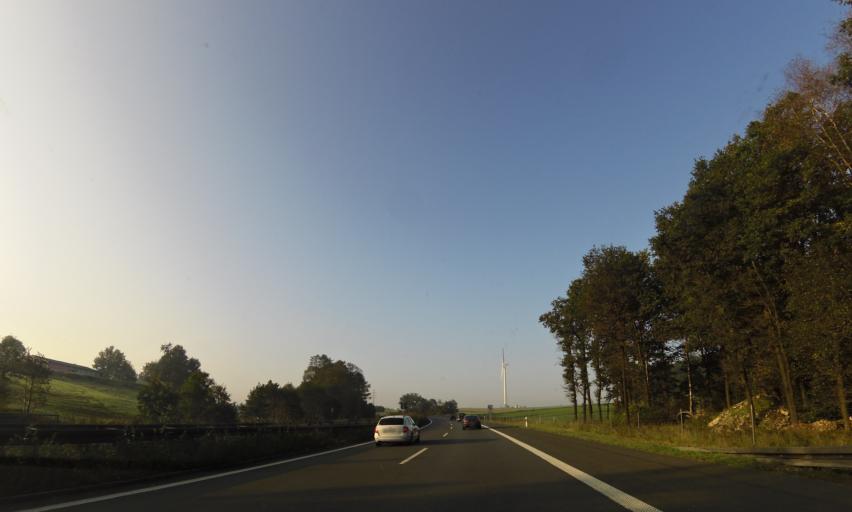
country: DE
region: Saxony
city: Treuen
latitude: 50.5740
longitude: 12.2878
